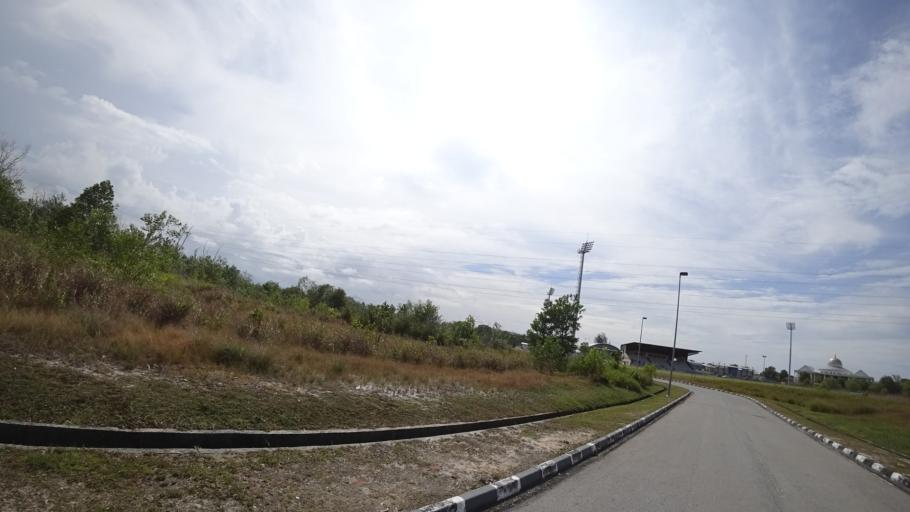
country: BN
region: Tutong
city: Tutong
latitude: 4.8123
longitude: 114.6611
